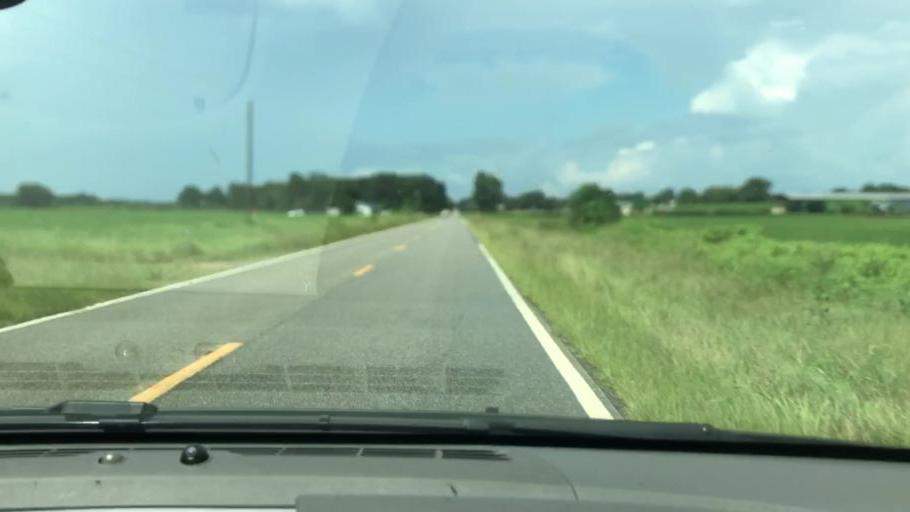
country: US
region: Georgia
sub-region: Seminole County
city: Donalsonville
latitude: 31.1127
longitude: -84.9958
